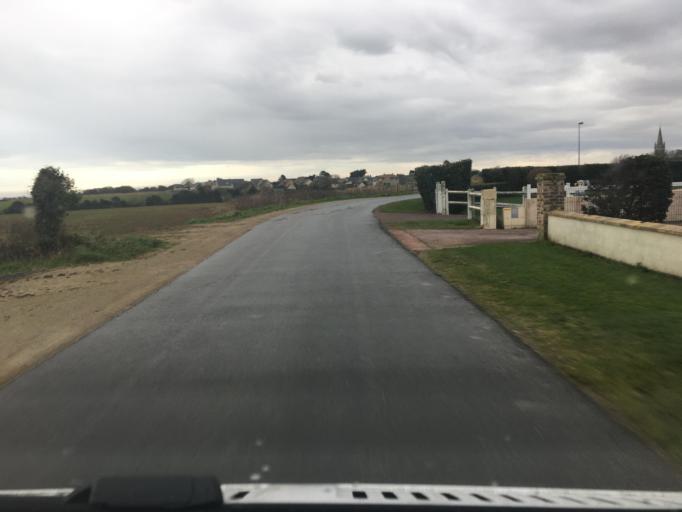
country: FR
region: Lower Normandy
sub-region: Departement du Calvados
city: Grandcamp-Maisy
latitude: 49.3769
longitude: -0.9086
